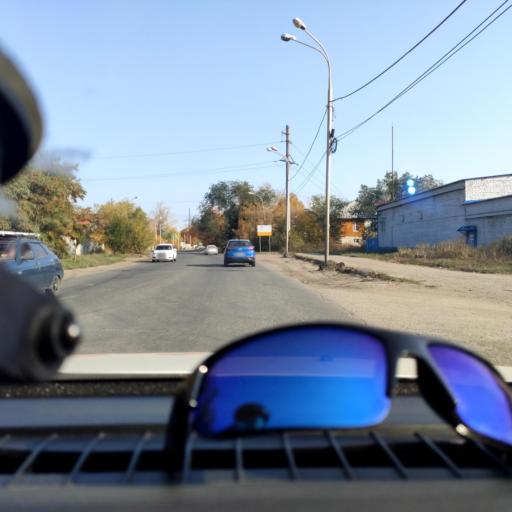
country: RU
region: Samara
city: Samara
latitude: 53.1340
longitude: 50.1194
